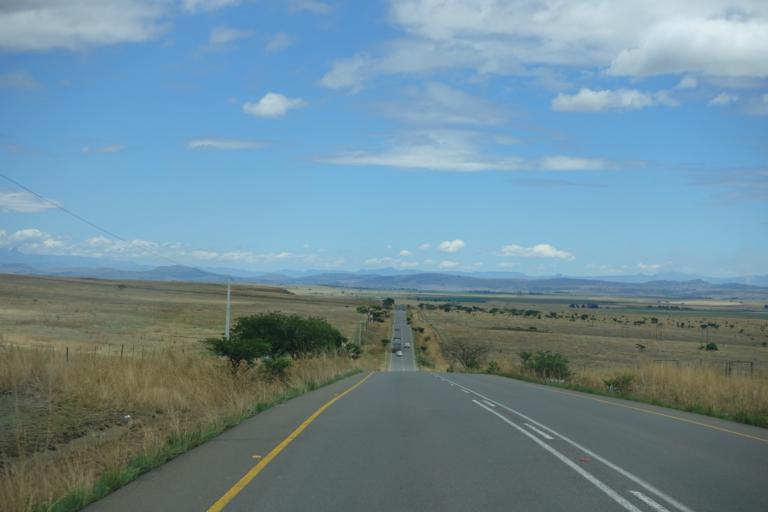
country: ZA
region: KwaZulu-Natal
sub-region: uThukela District Municipality
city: Estcourt
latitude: -28.8720
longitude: 29.7173
